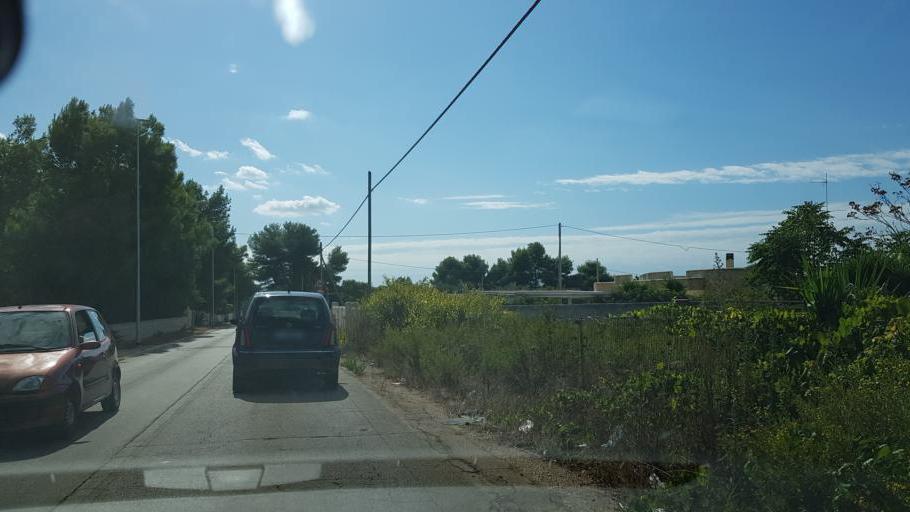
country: IT
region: Apulia
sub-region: Provincia di Lecce
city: Porto Cesareo
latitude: 40.2391
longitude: 17.9164
